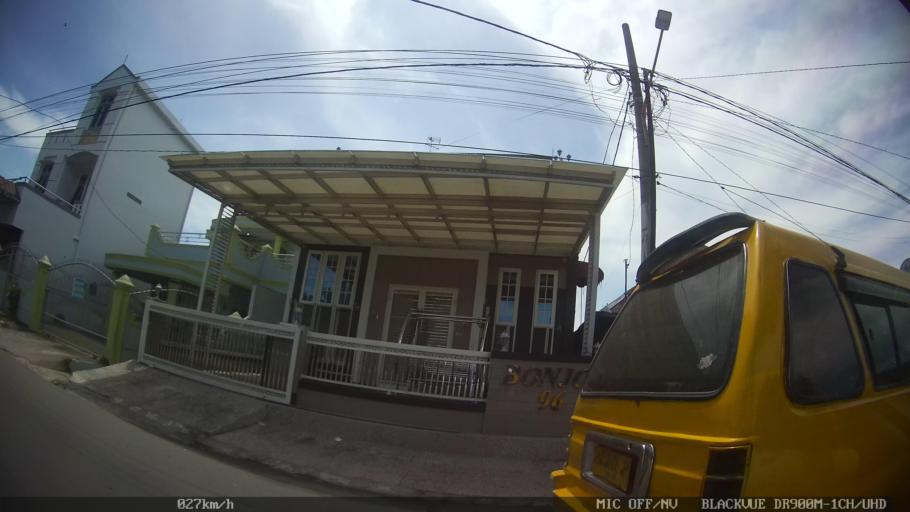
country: ID
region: North Sumatra
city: Binjai
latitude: 3.6059
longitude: 98.4903
